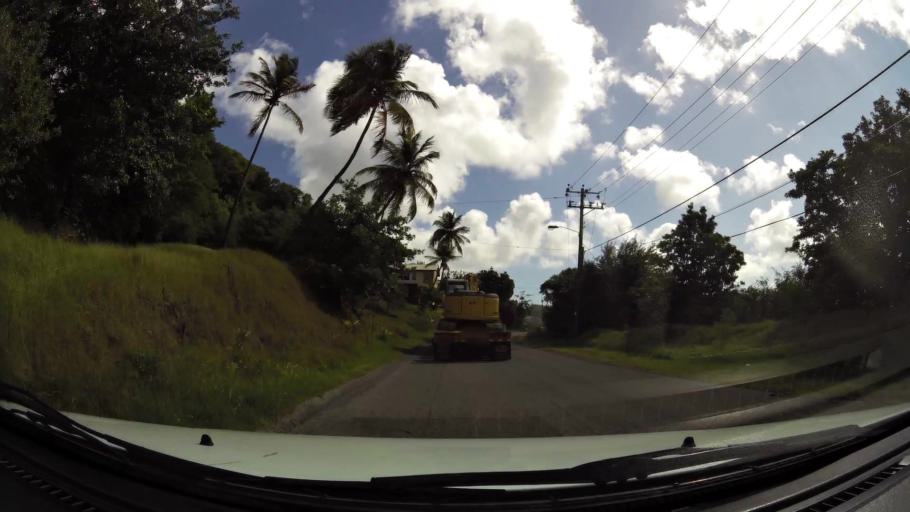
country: LC
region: Laborie Quarter
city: Laborie
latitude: 13.7523
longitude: -61.0046
